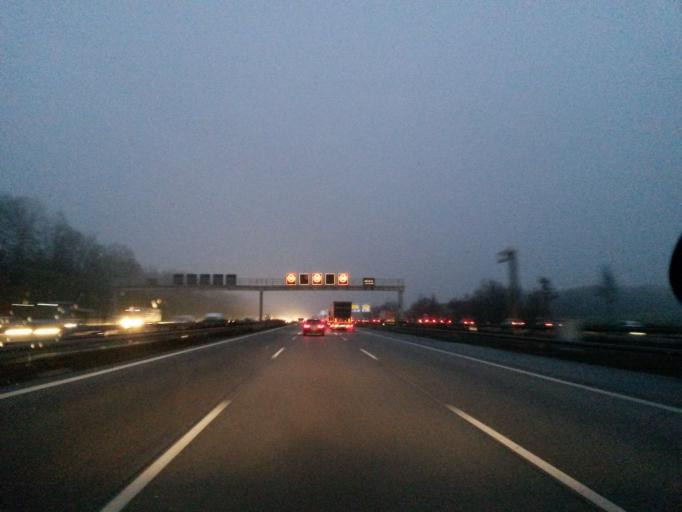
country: DE
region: Baden-Wuerttemberg
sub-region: Regierungsbezirk Stuttgart
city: Leinfelden-Echterdingen
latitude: 48.7082
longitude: 9.1509
